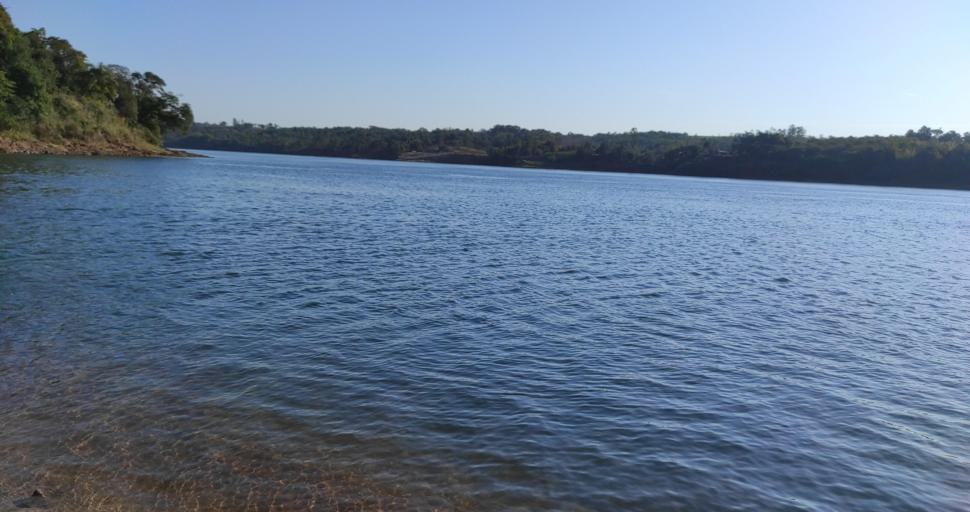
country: AR
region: Misiones
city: Capiovi
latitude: -26.8637
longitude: -55.1365
